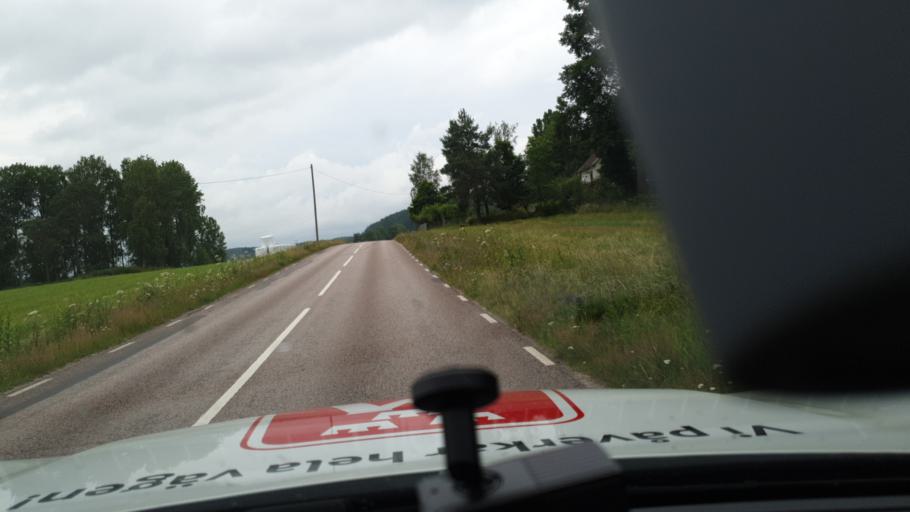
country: SE
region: Vaermland
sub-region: Sunne Kommun
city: Sunne
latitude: 59.8026
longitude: 13.2271
